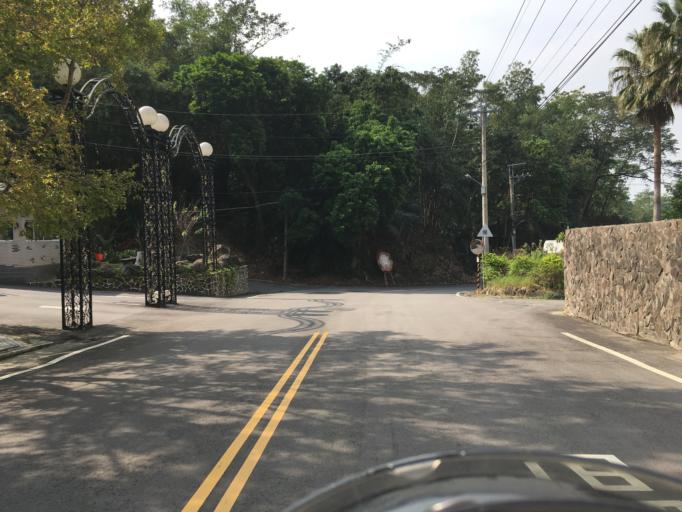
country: TW
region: Taiwan
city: Fengyuan
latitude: 24.1844
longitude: 120.7651
